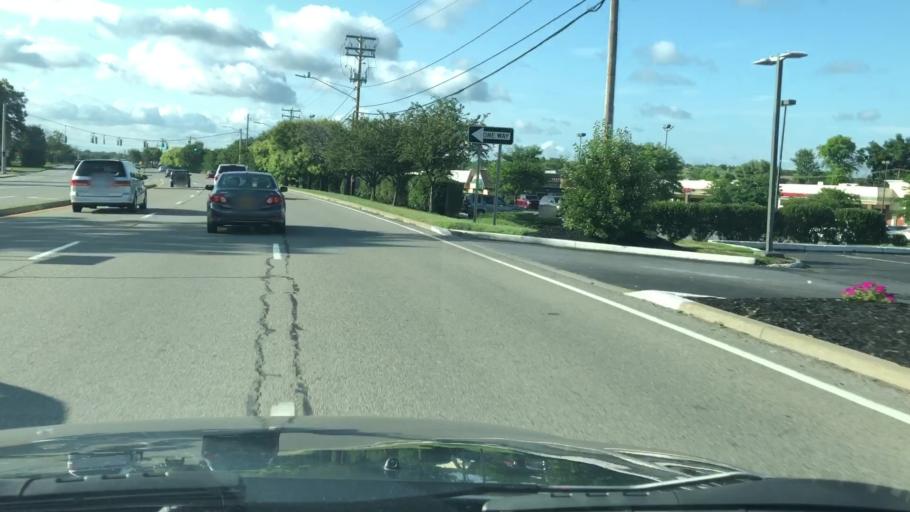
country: US
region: New York
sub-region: Dutchess County
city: Wappingers Falls
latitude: 41.5893
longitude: -73.9076
